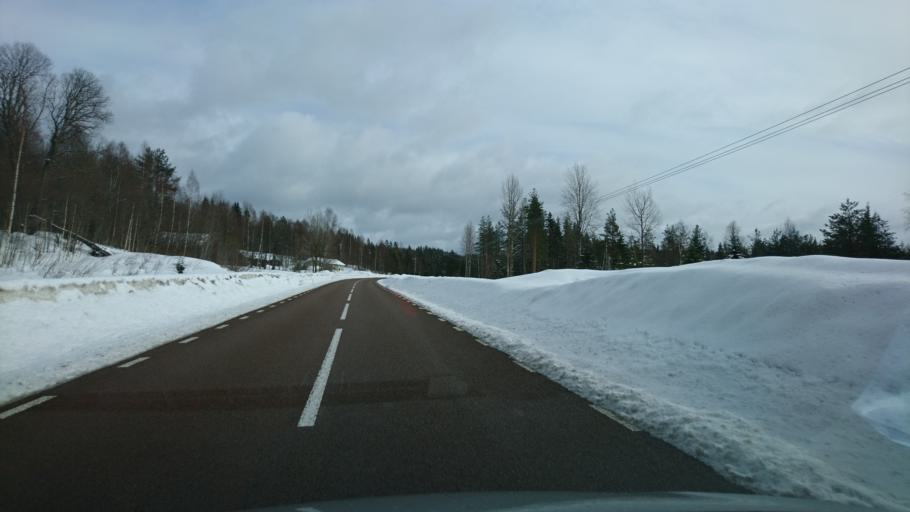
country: SE
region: Vaesternorrland
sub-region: Solleftea Kommun
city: Solleftea
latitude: 62.8730
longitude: 17.2934
